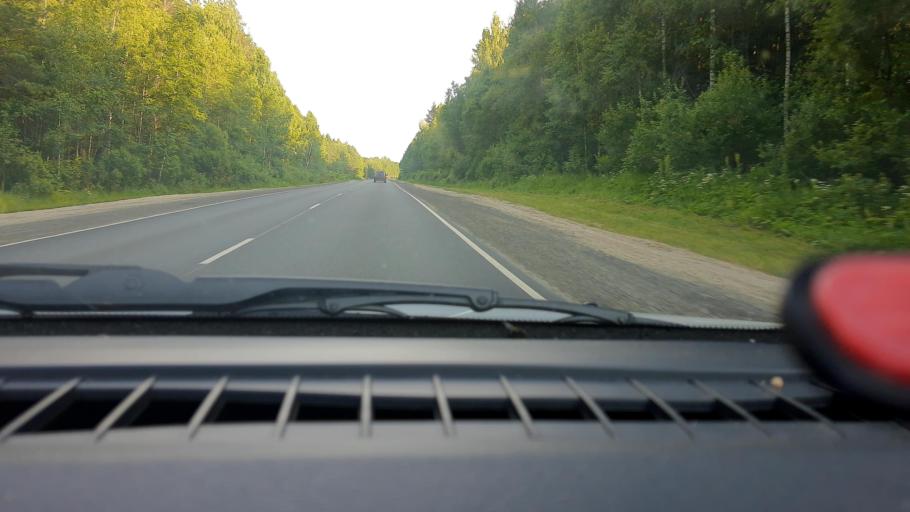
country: RU
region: Nizjnij Novgorod
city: Arzamas
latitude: 55.4255
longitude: 43.9063
